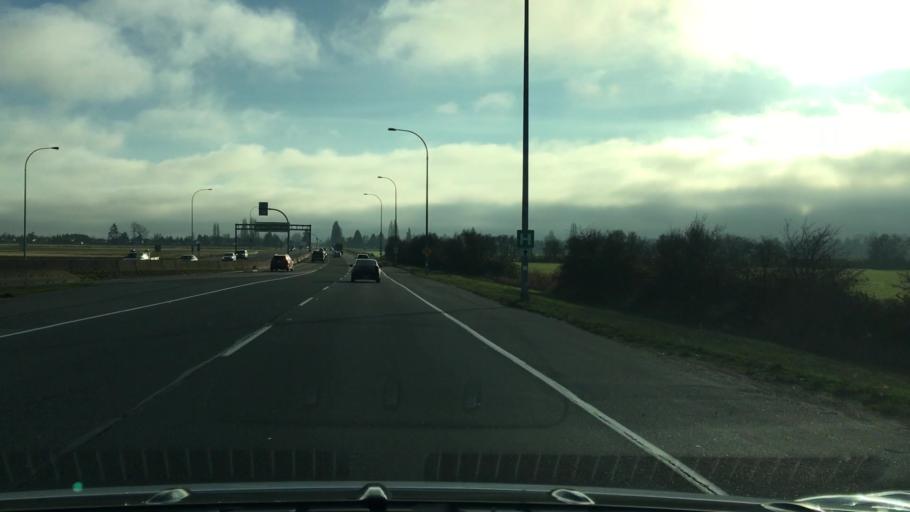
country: CA
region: British Columbia
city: Ladner
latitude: 49.1065
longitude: -123.0575
